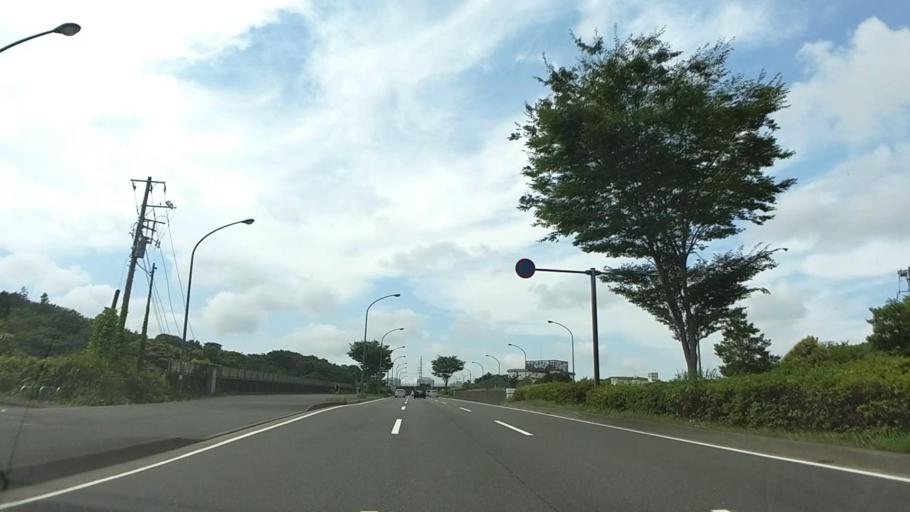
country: JP
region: Kanagawa
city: Yokohama
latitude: 35.4444
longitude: 139.5603
